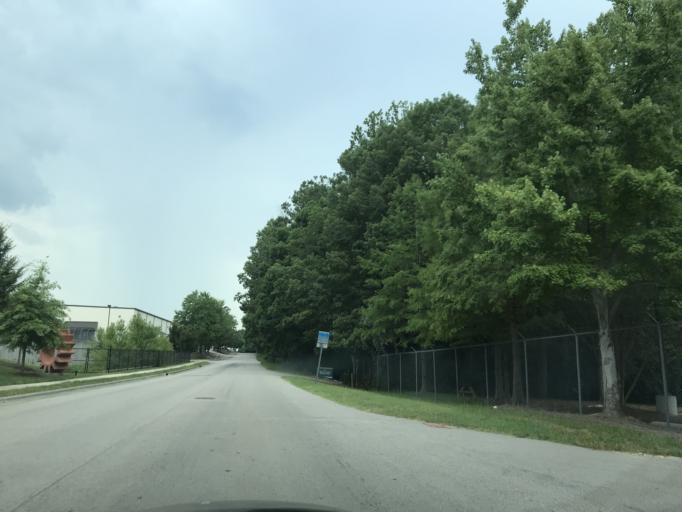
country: US
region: North Carolina
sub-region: Wake County
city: Wake Forest
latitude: 35.8892
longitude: -78.5778
